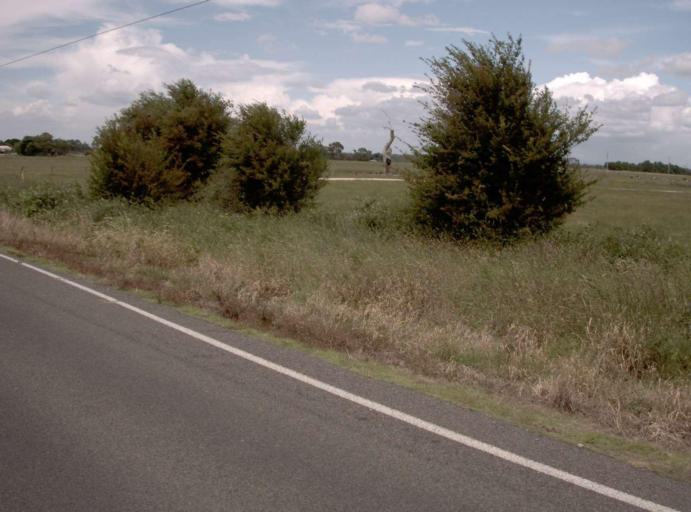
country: AU
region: Victoria
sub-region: Wellington
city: Sale
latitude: -38.0224
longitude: 147.0114
